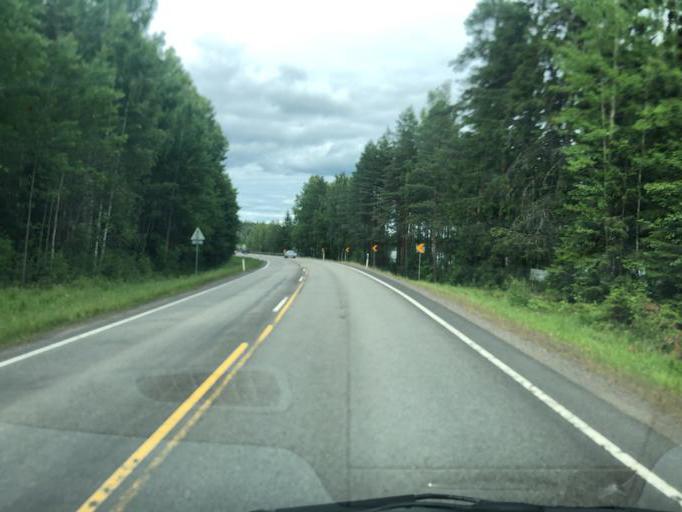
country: FI
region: Kymenlaakso
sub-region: Kouvola
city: Kouvola
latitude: 60.9567
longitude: 26.8612
